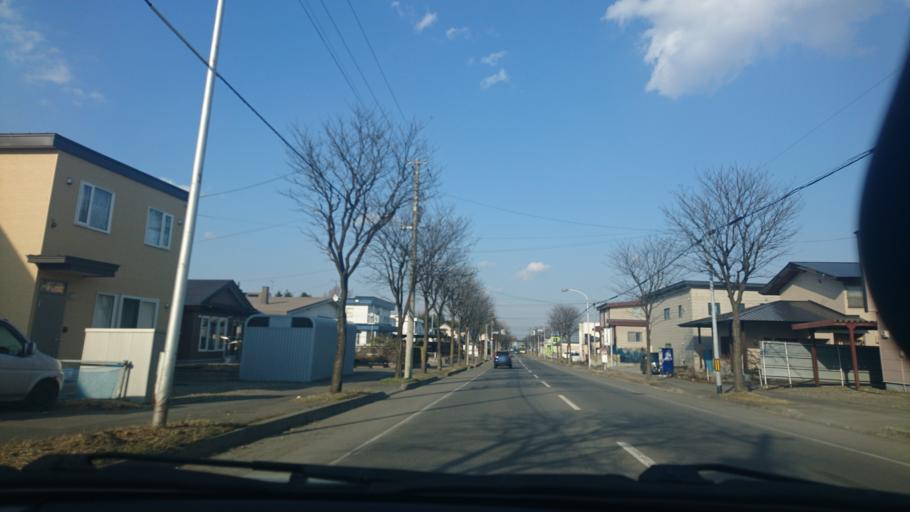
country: JP
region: Hokkaido
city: Obihiro
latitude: 42.9233
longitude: 143.1583
